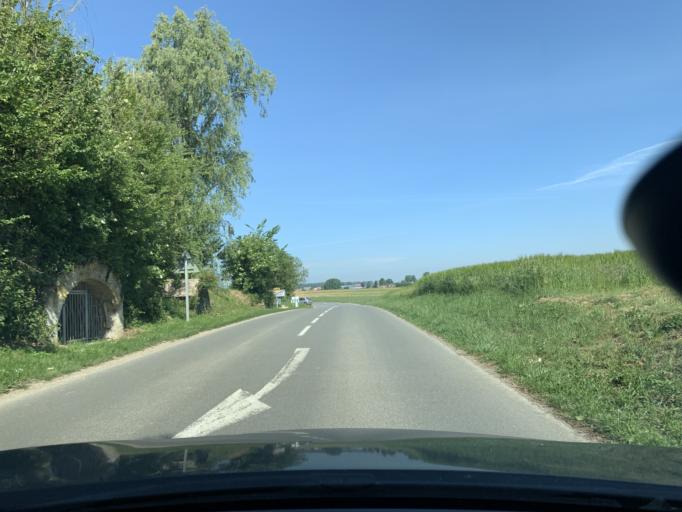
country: FR
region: Nord-Pas-de-Calais
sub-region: Departement du Nord
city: Marcoing
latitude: 50.1412
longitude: 3.1757
